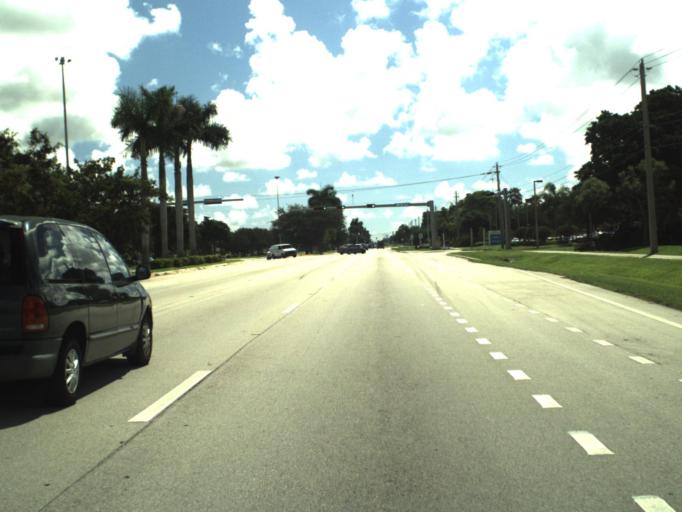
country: US
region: Florida
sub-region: Broward County
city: Miramar
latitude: 26.0087
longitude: -80.2592
